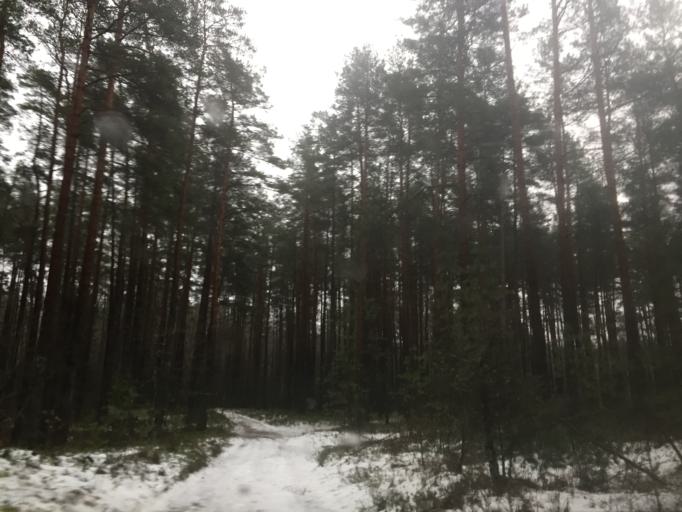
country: LV
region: Stopini
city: Ulbroka
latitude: 56.9534
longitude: 24.3366
